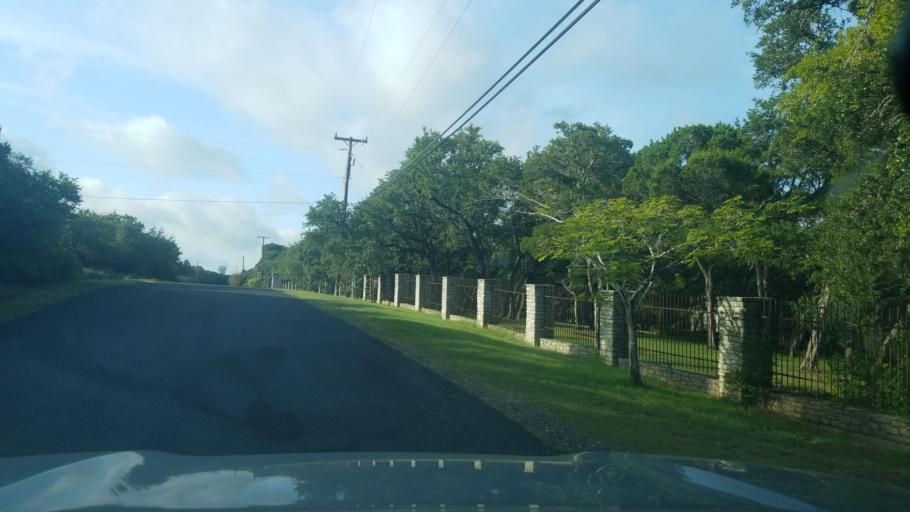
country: US
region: Texas
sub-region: Bexar County
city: Timberwood Park
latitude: 29.7045
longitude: -98.5192
